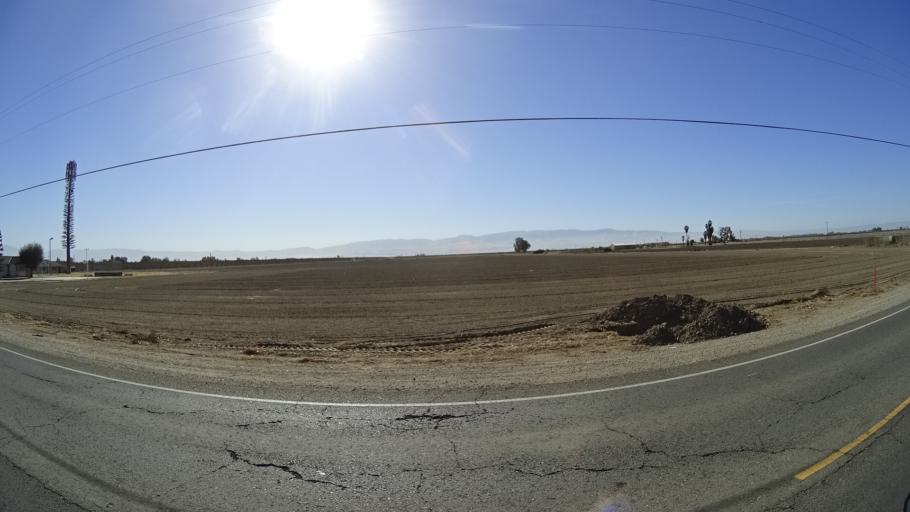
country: US
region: California
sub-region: Kern County
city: Greenfield
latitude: 35.2670
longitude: -119.0449
